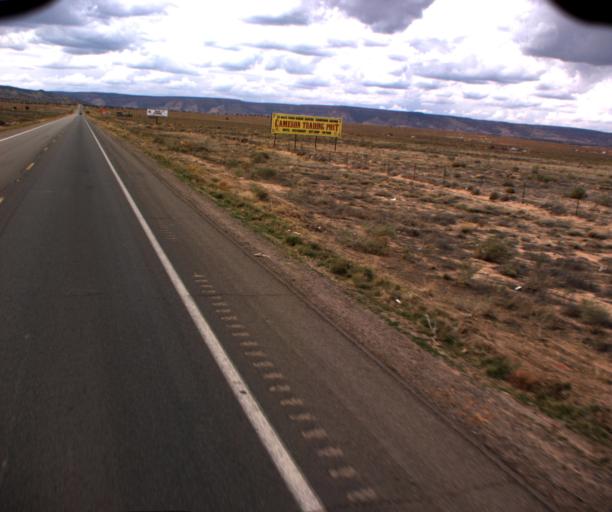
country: US
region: Arizona
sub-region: Navajo County
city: Kayenta
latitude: 36.7054
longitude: -110.2629
